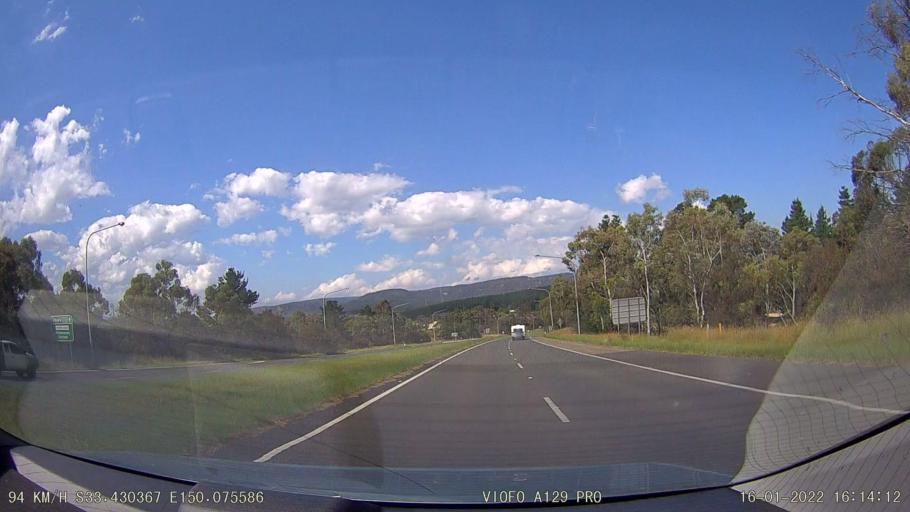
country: AU
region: New South Wales
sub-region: Lithgow
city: Lithgow
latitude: -33.4305
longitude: 150.0754
